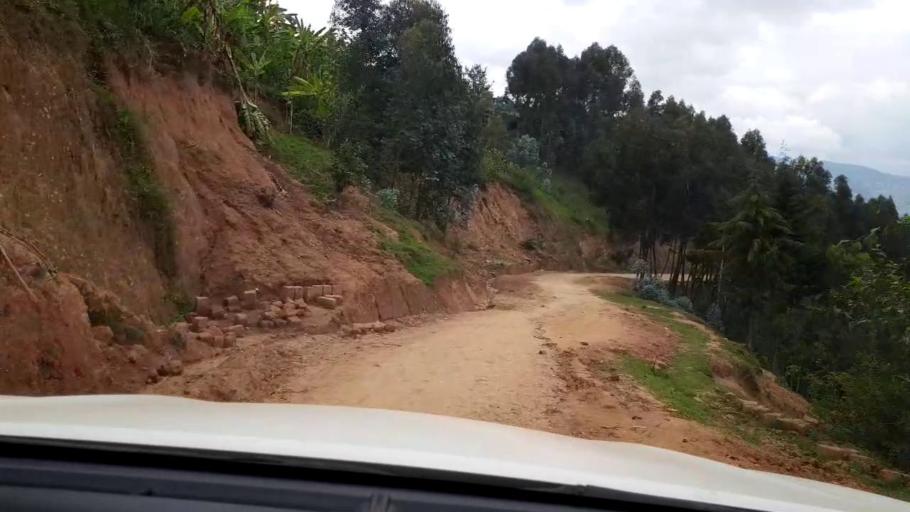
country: RW
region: Western Province
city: Kibuye
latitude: -1.8275
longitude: 29.5484
